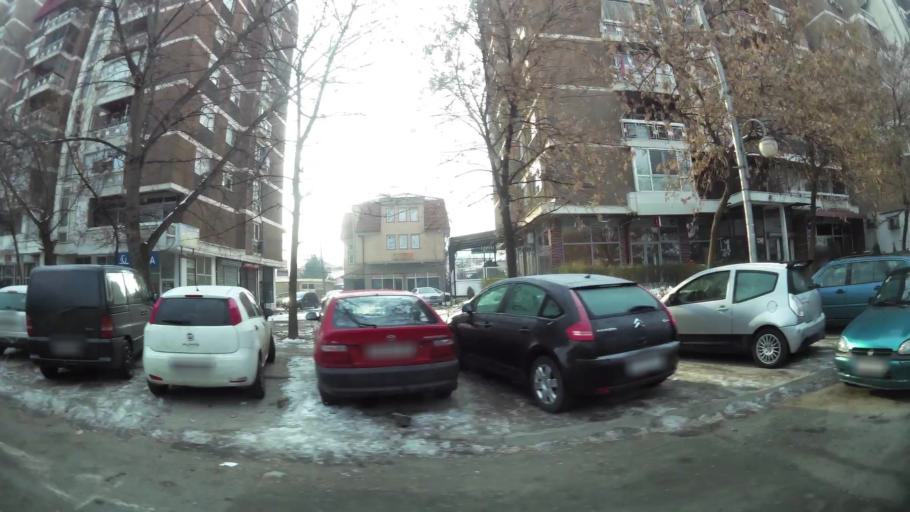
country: MK
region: Cair
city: Cair
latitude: 42.0130
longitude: 21.4346
